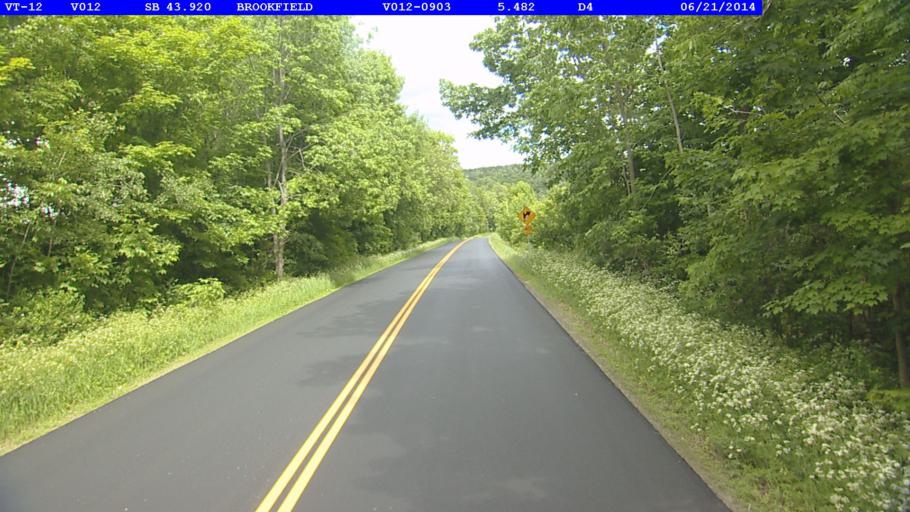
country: US
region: Vermont
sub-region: Washington County
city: Northfield
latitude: 44.0761
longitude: -72.6419
